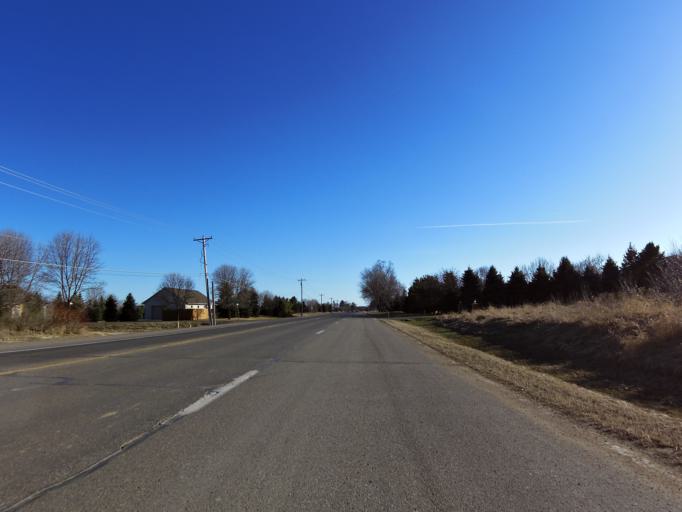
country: US
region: Wisconsin
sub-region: Saint Croix County
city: North Hudson
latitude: 44.9852
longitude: -92.7904
